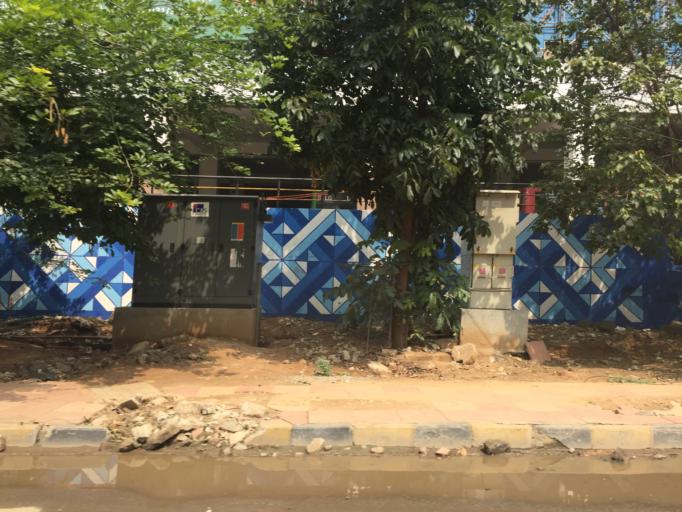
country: IN
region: Karnataka
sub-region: Bangalore Rural
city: Hoskote
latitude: 12.9770
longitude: 77.7272
